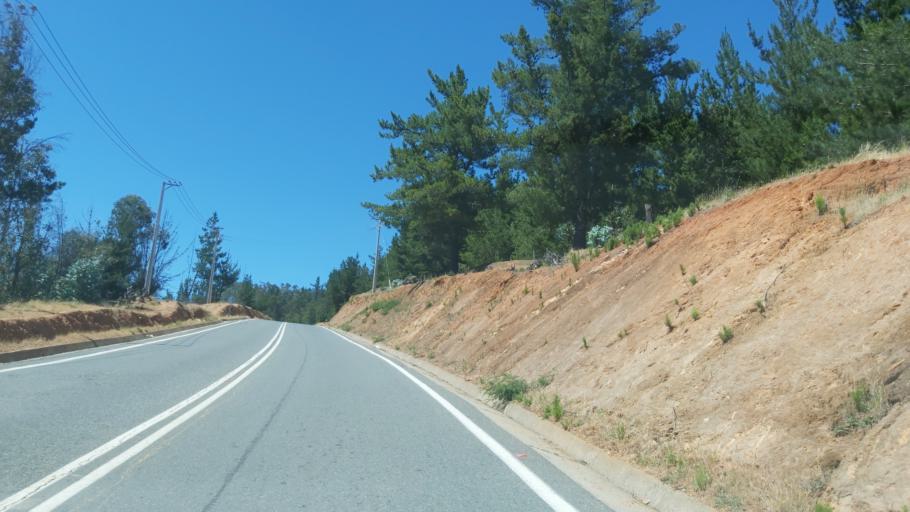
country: CL
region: Maule
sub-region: Provincia de Talca
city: Constitucion
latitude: -34.9124
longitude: -71.9961
